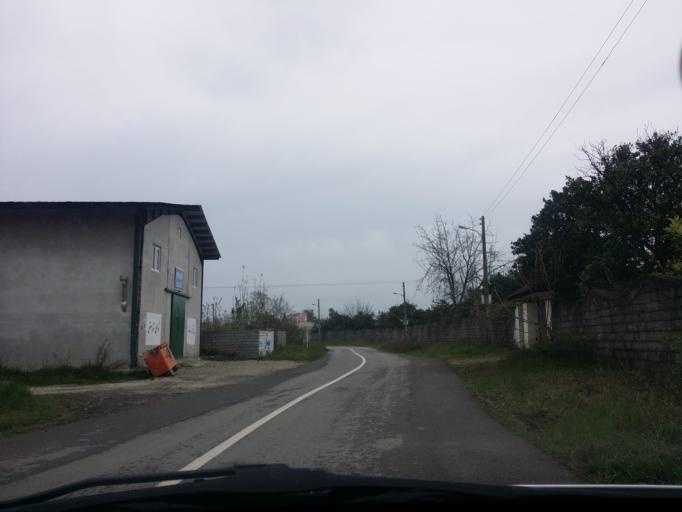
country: IR
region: Mazandaran
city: Chalus
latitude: 36.6850
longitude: 51.3796
